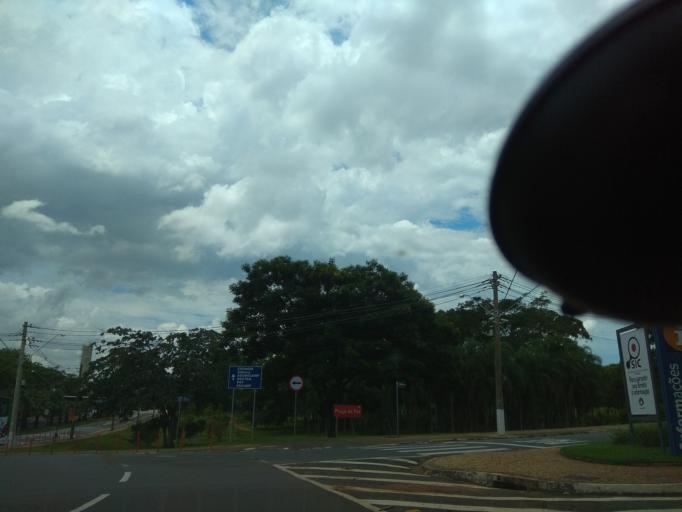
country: BR
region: Sao Paulo
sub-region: Campinas
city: Campinas
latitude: -22.8223
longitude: -47.0697
